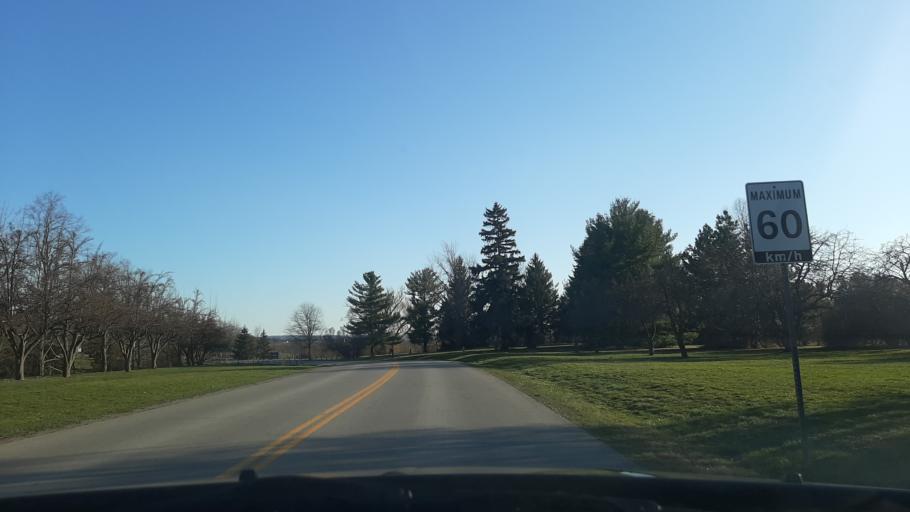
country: US
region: New York
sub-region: Niagara County
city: Youngstown
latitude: 43.2336
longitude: -79.0616
